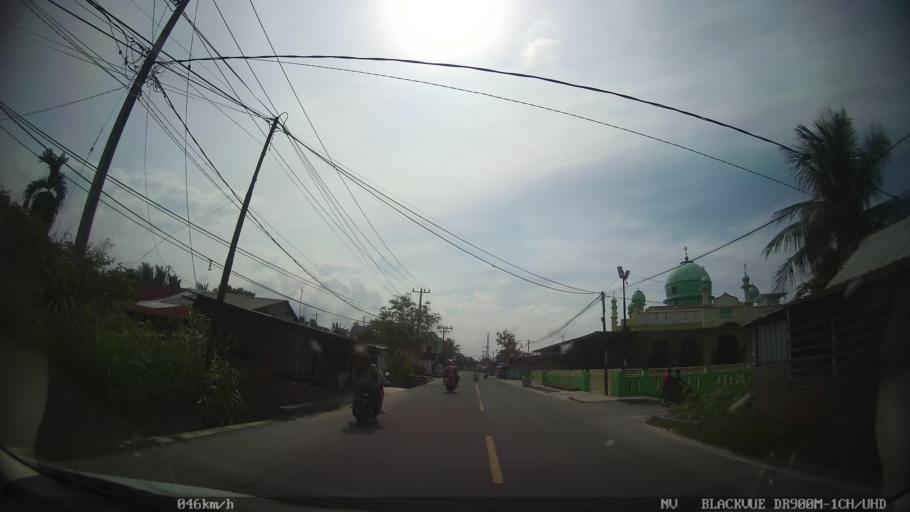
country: ID
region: North Sumatra
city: Percut
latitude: 3.6120
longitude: 98.8105
